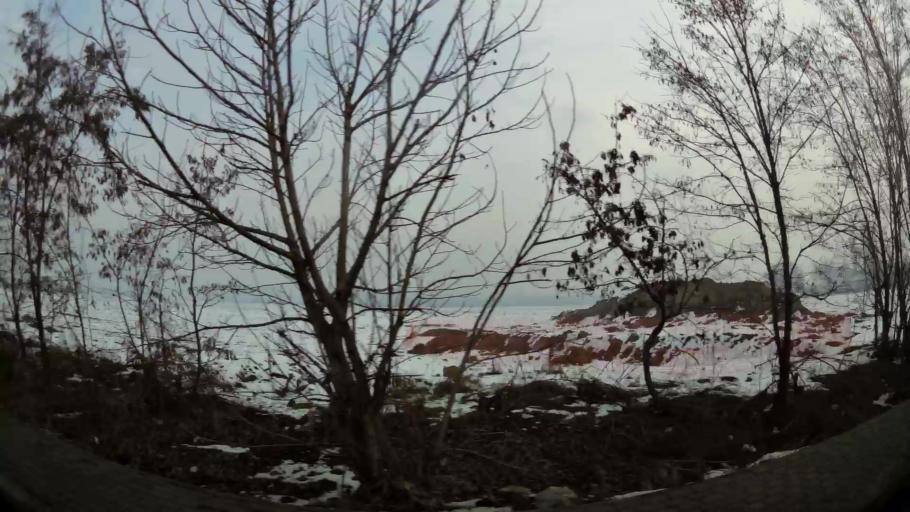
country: MK
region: Ilinden
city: Jurumleri
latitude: 41.9845
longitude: 21.5211
